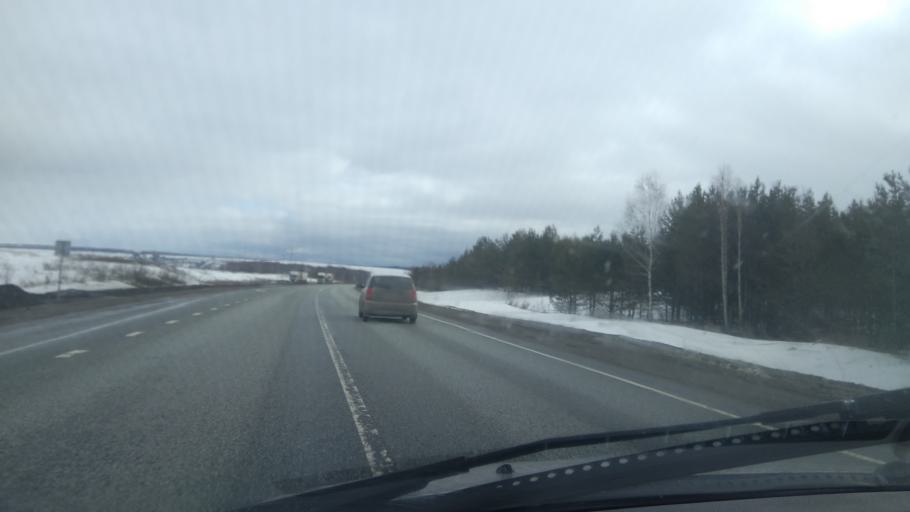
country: RU
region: Sverdlovsk
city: Achit
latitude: 56.7972
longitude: 57.8628
